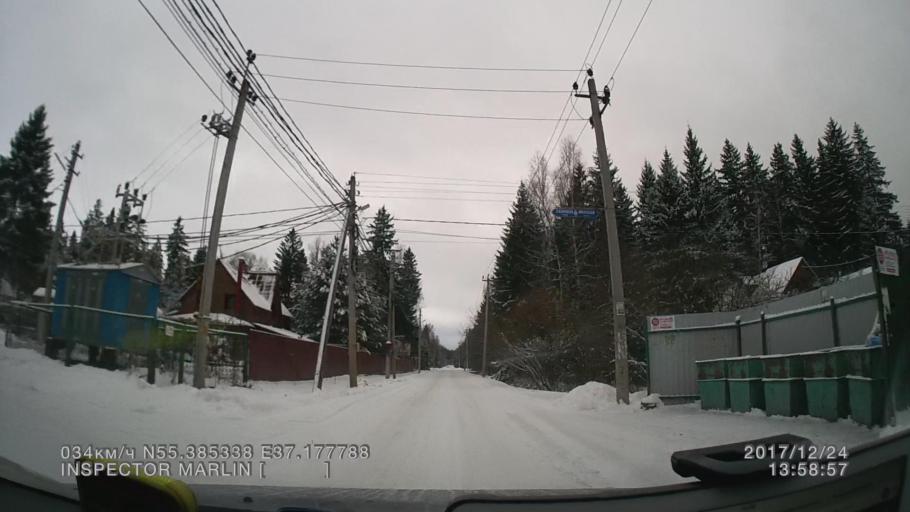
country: RU
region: Moskovskaya
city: Troitsk
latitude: 55.3853
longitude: 37.1778
